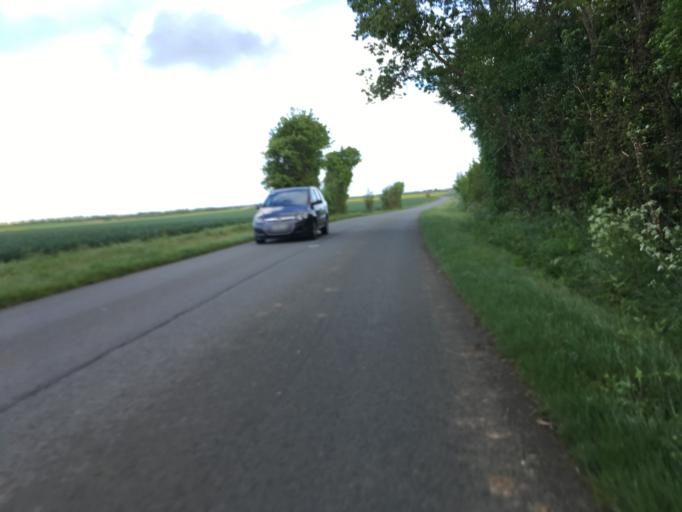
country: FR
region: Poitou-Charentes
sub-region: Departement de la Charente-Maritime
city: Sainte-Soulle
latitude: 46.1748
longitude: -0.9947
